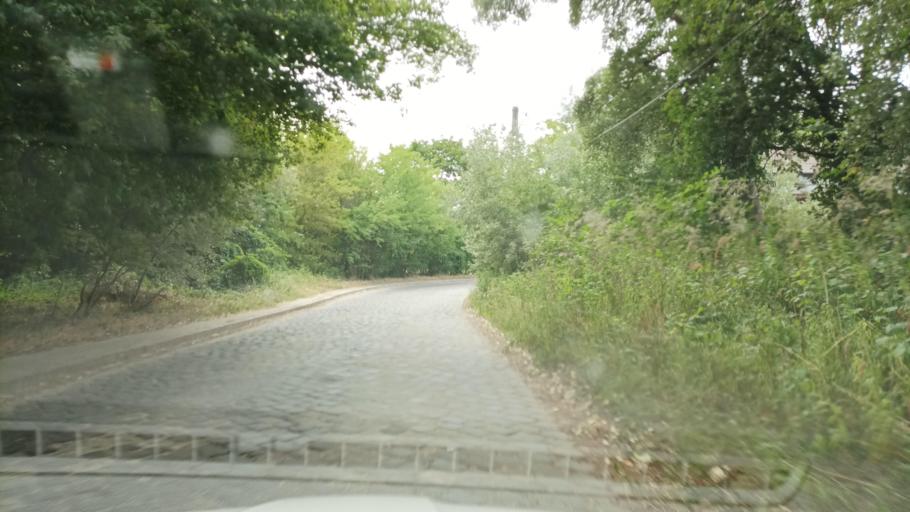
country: HU
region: Pest
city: Vac
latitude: 47.7741
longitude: 19.1186
